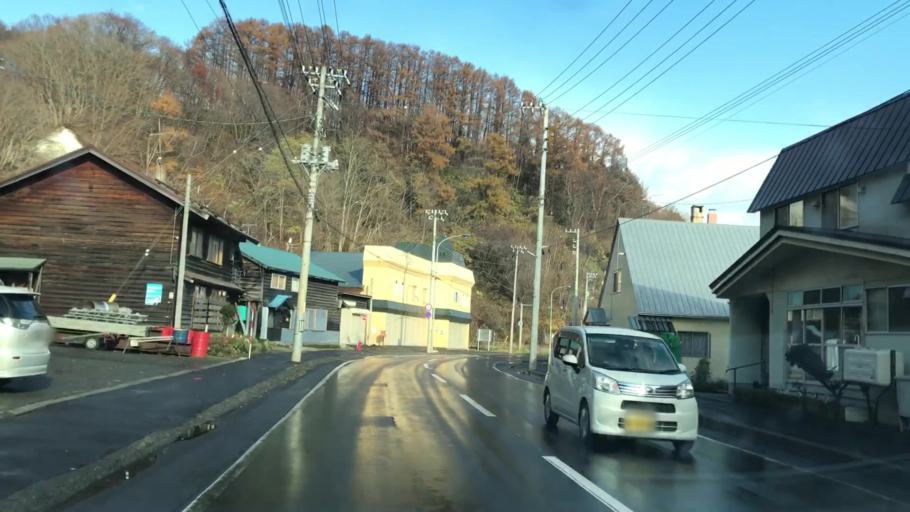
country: JP
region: Hokkaido
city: Yoichi
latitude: 43.2740
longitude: 140.6354
